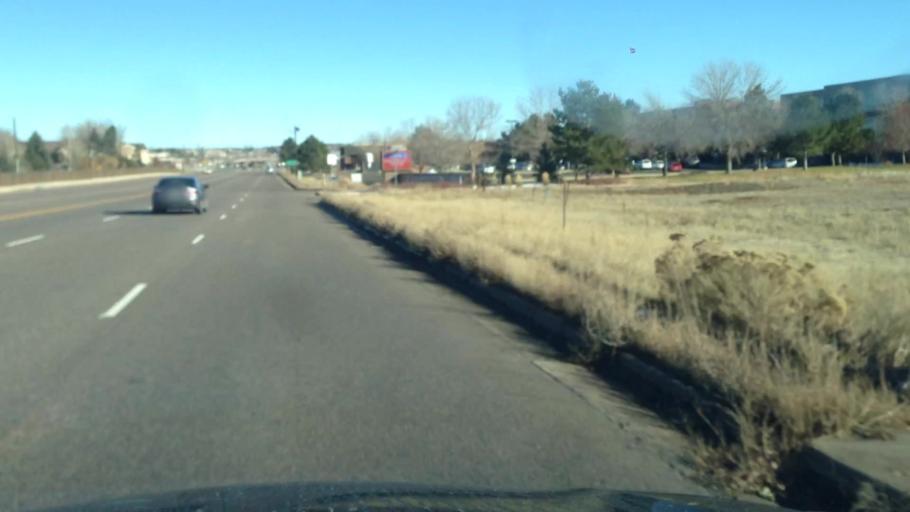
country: US
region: Colorado
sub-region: Arapahoe County
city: Dove Valley
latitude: 39.5948
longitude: -104.8272
